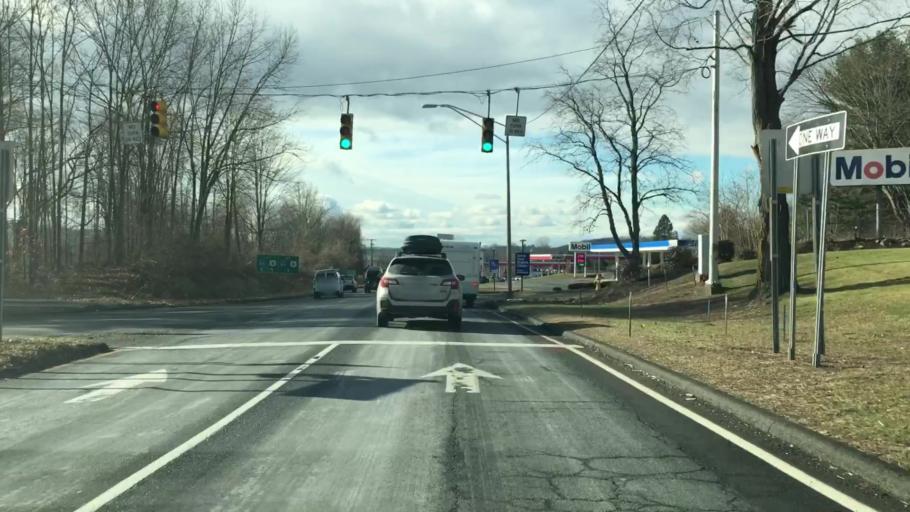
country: US
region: Connecticut
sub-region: Fairfield County
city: Bethel
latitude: 41.4181
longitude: -73.4055
